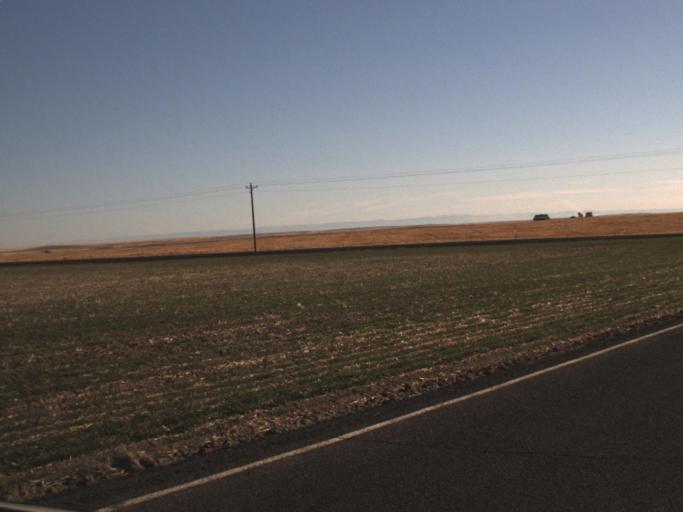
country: US
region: Washington
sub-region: Adams County
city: Ritzville
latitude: 46.8248
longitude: -118.5468
